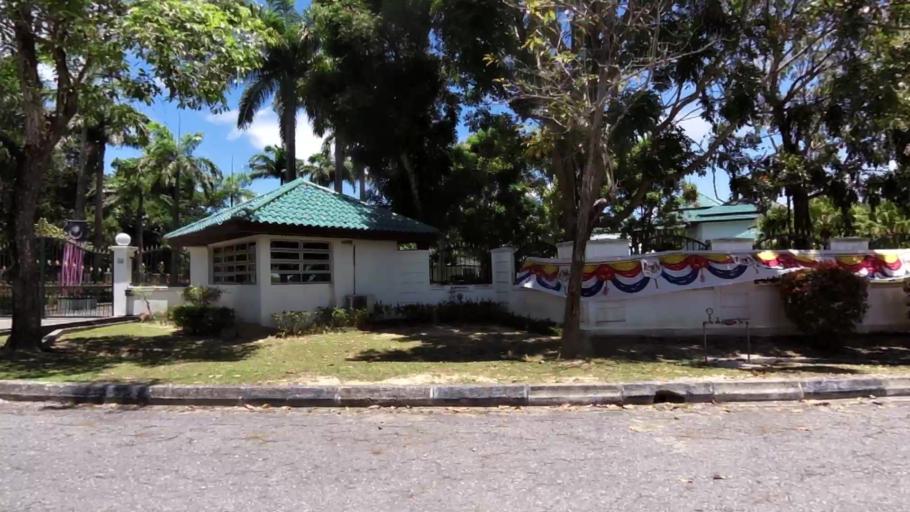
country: BN
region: Brunei and Muara
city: Bandar Seri Begawan
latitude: 4.9225
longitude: 114.9656
